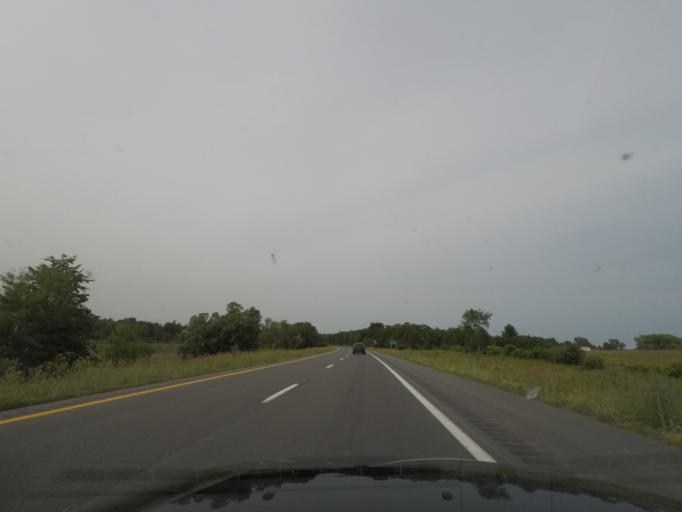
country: US
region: New York
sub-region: Clinton County
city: Cumberland Head
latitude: 44.7445
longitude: -73.4280
